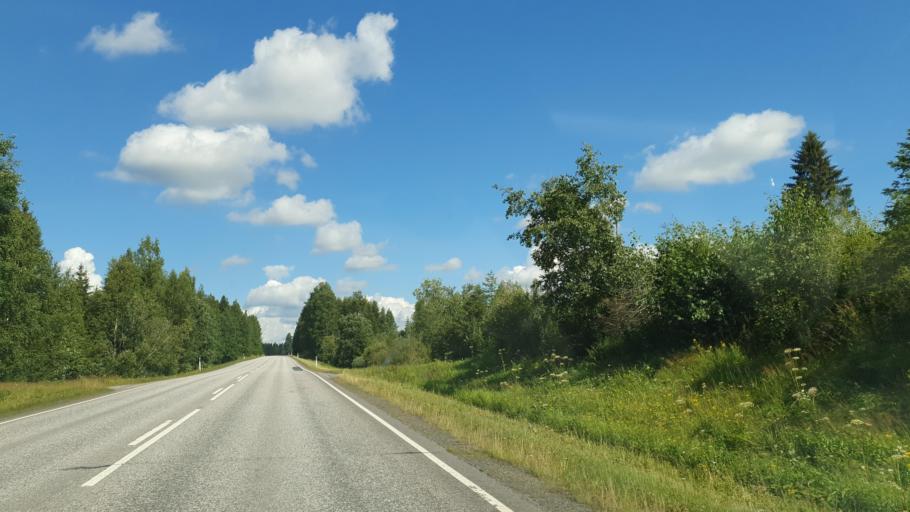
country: FI
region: Northern Savo
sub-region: Ylae-Savo
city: Sonkajaervi
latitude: 63.7365
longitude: 27.3789
